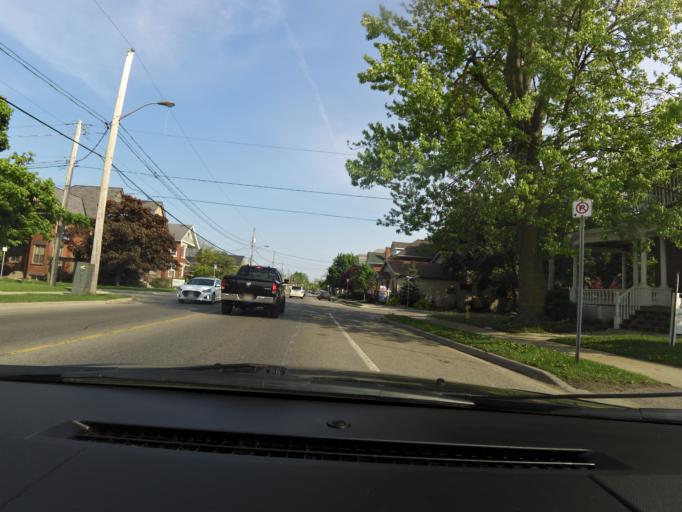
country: CA
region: Ontario
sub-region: Wellington County
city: Guelph
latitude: 43.5521
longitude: -80.2596
